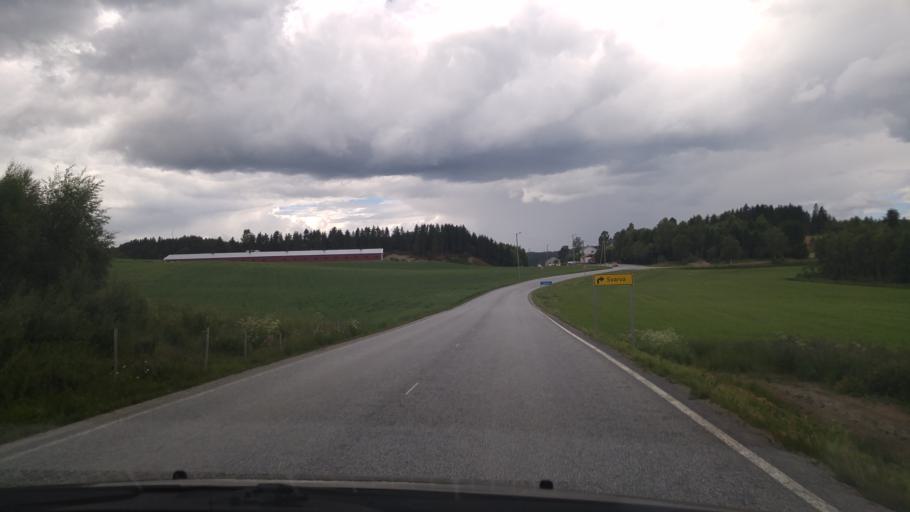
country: NO
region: Nord-Trondelag
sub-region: Steinkjer
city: Steinkjer
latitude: 64.0955
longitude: 11.4569
